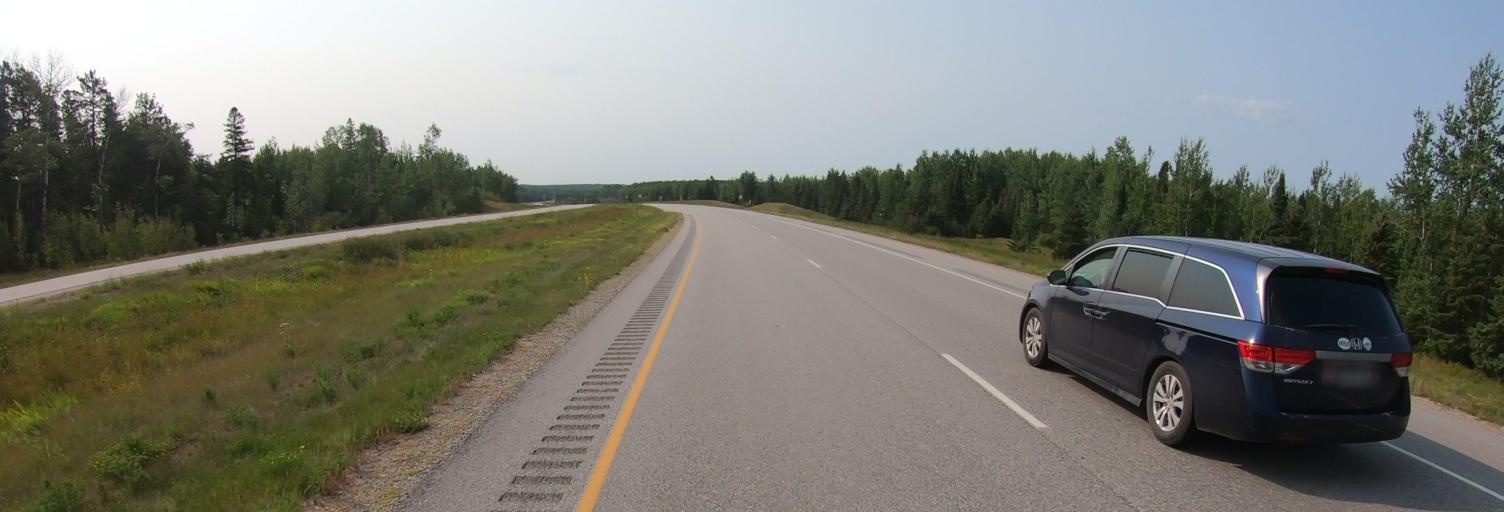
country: US
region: Minnesota
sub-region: Saint Louis County
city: Mountain Iron
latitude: 47.7187
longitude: -92.6515
